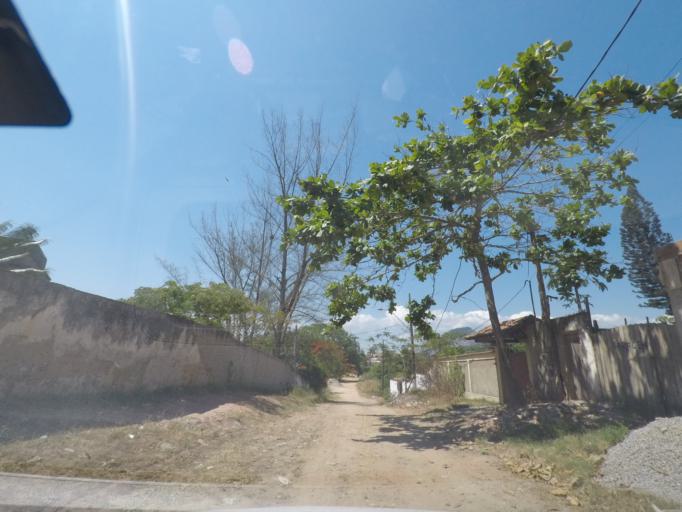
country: BR
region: Rio de Janeiro
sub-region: Marica
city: Marica
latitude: -22.9736
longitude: -42.9280
